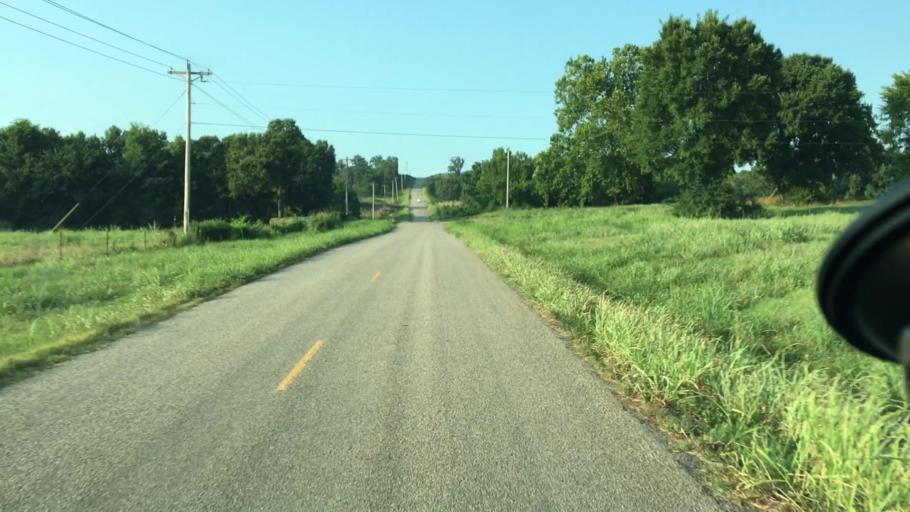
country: US
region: Arkansas
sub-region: Johnson County
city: Coal Hill
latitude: 35.3637
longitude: -93.6130
